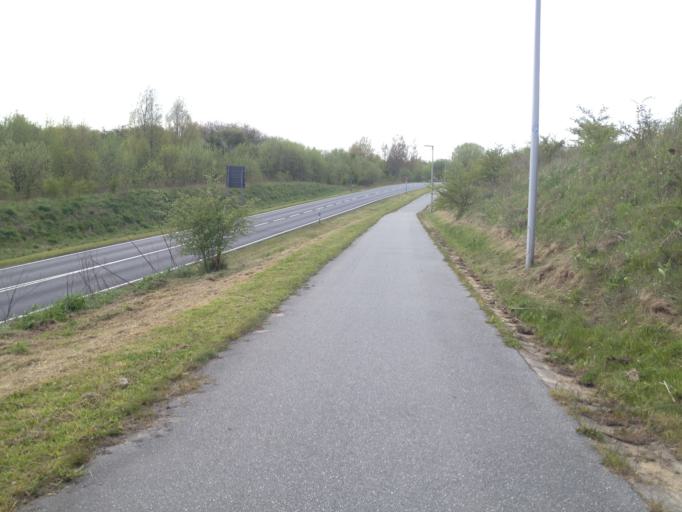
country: DE
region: Schleswig-Holstein
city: Flensburg
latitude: 54.7706
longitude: 9.4587
